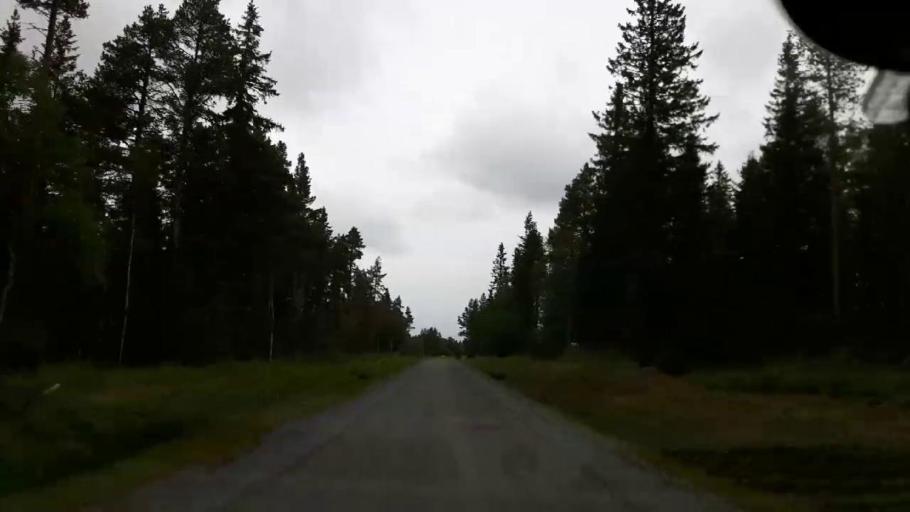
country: SE
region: Jaemtland
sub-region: OEstersunds Kommun
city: Ostersund
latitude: 63.0845
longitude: 14.5551
